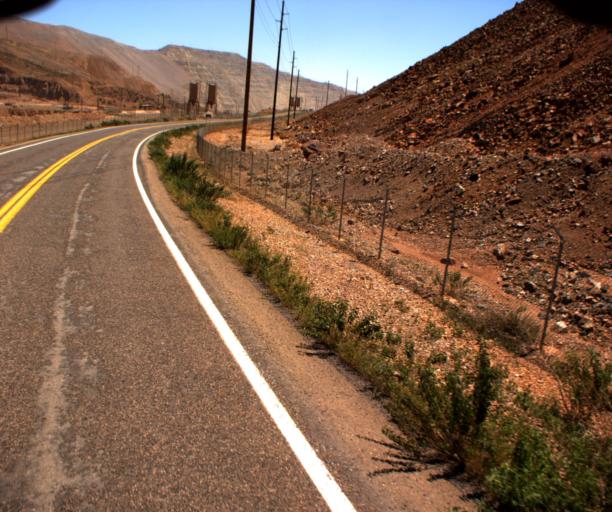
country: US
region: Arizona
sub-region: Greenlee County
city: Morenci
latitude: 33.1279
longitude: -109.3709
